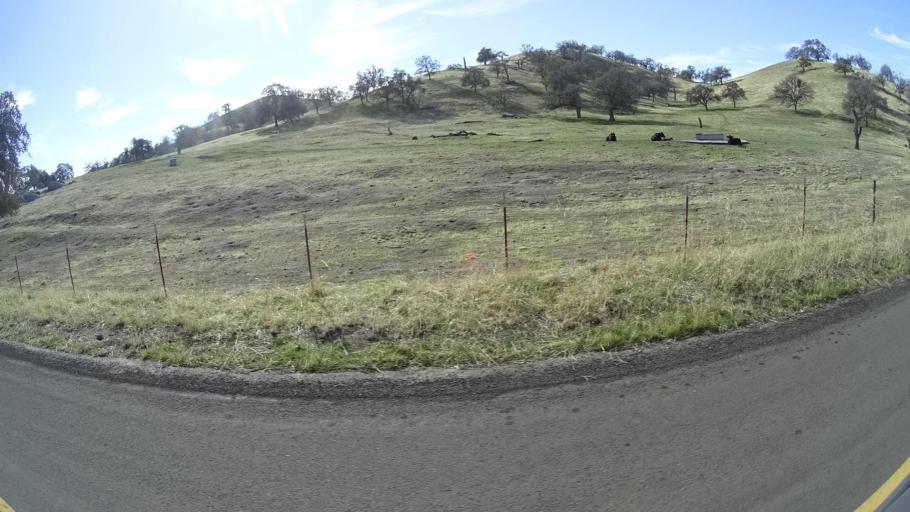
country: US
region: California
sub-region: Tulare County
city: Richgrove
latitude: 35.6708
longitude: -118.8508
